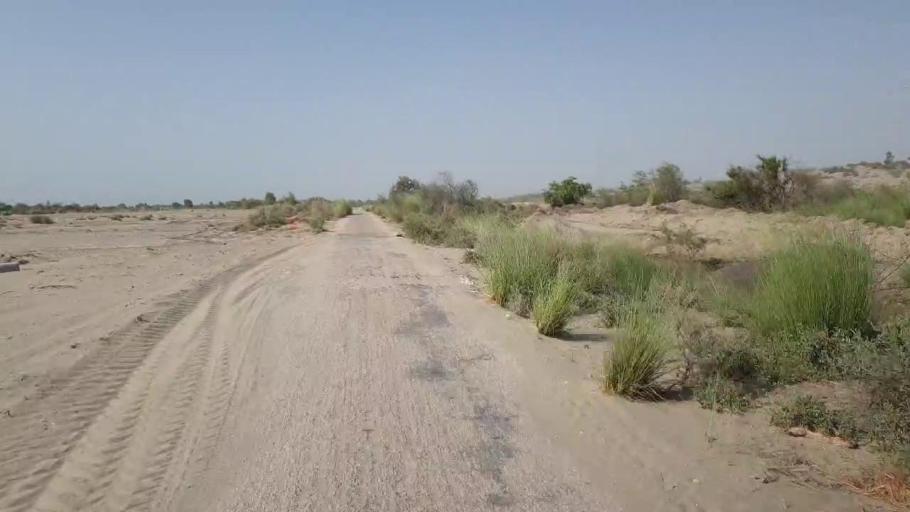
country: PK
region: Sindh
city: Jam Sahib
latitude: 26.6007
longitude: 68.9254
